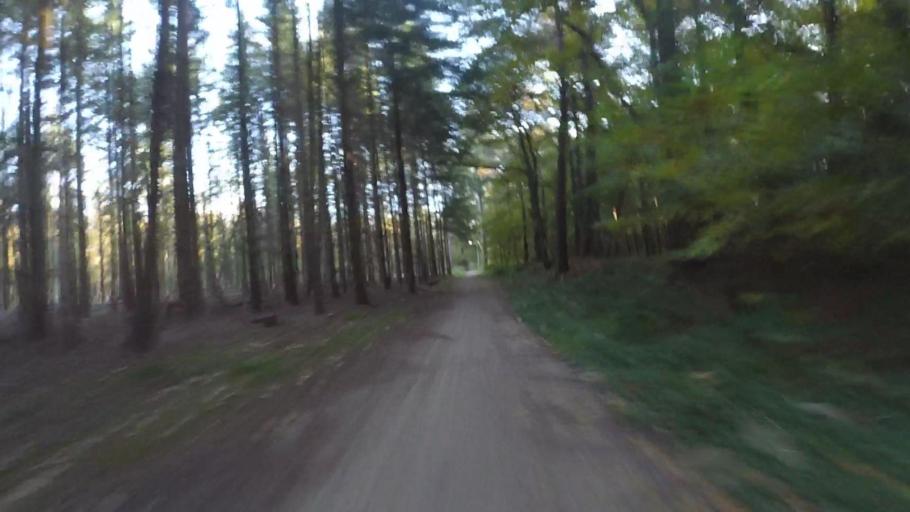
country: NL
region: Utrecht
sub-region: Gemeente Baarn
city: Baarn
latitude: 52.1922
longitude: 5.2405
